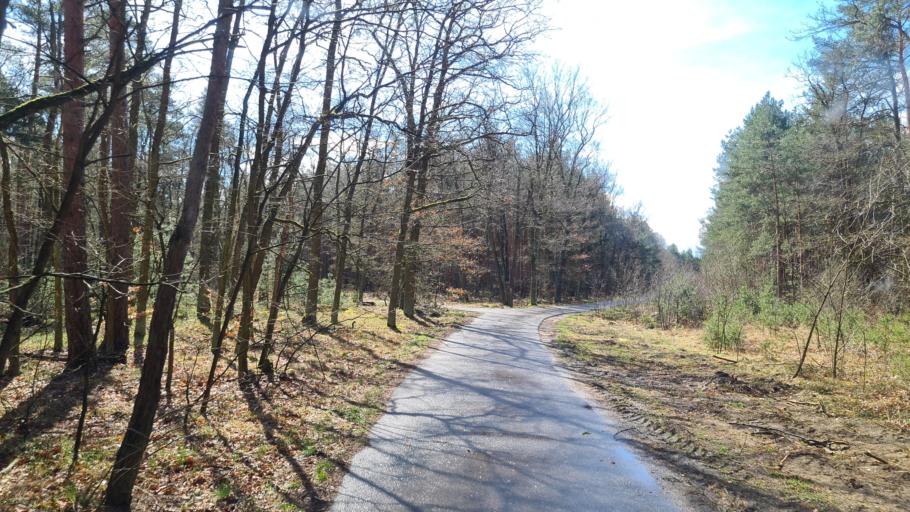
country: DE
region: Brandenburg
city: Altdobern
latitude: 51.7032
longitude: 14.0379
